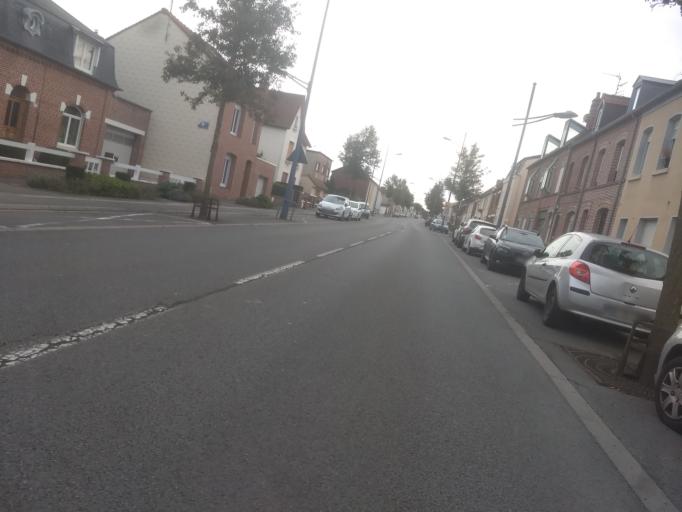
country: FR
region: Nord-Pas-de-Calais
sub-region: Departement du Pas-de-Calais
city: Beaurains
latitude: 50.2694
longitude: 2.7844
